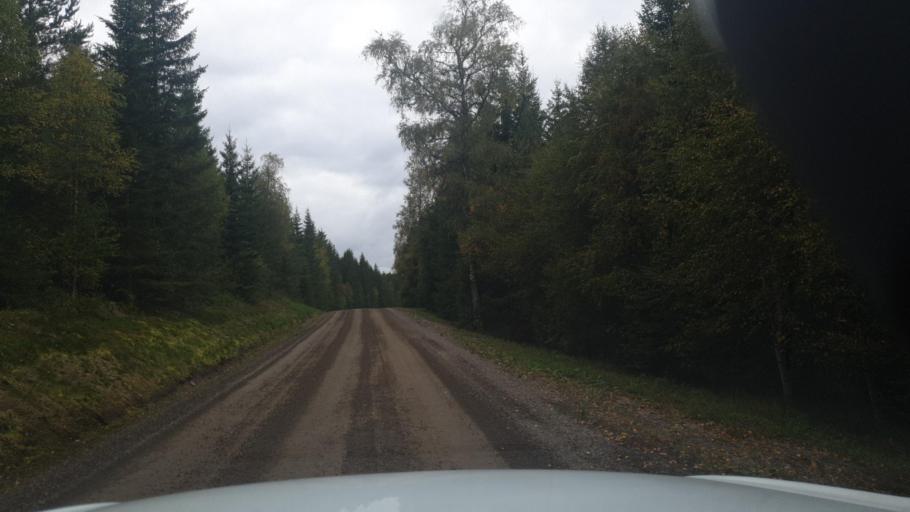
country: SE
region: Vaermland
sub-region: Sunne Kommun
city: Sunne
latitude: 59.8236
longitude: 12.8724
